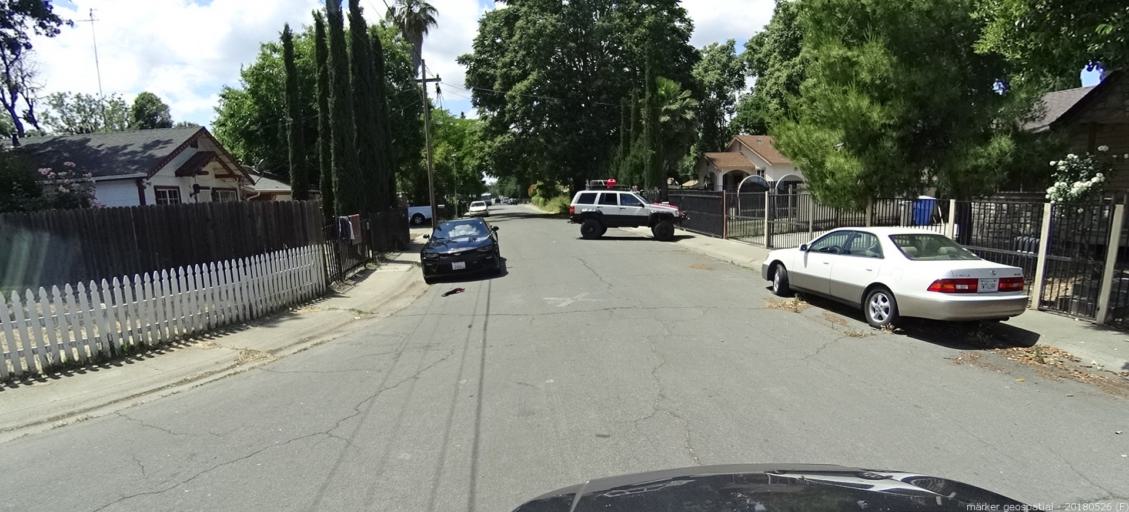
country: US
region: California
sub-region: Sacramento County
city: Sacramento
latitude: 38.6067
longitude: -121.4704
